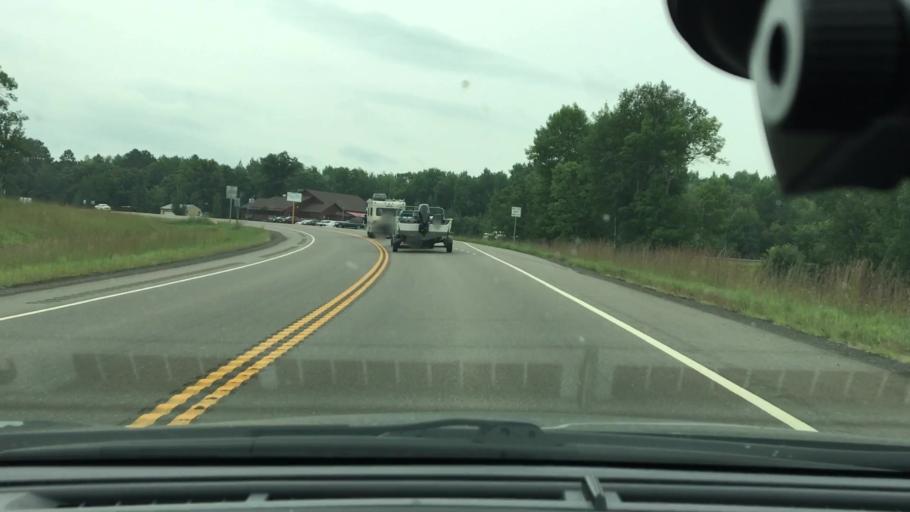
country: US
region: Minnesota
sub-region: Crow Wing County
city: Crosby
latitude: 46.5474
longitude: -93.9583
